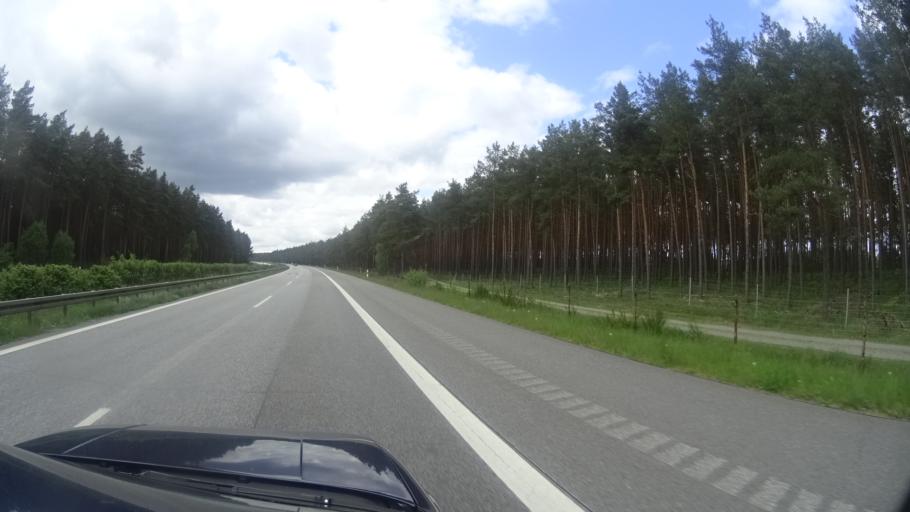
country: DE
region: Mecklenburg-Vorpommern
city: Malchow
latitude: 53.5342
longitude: 12.3494
